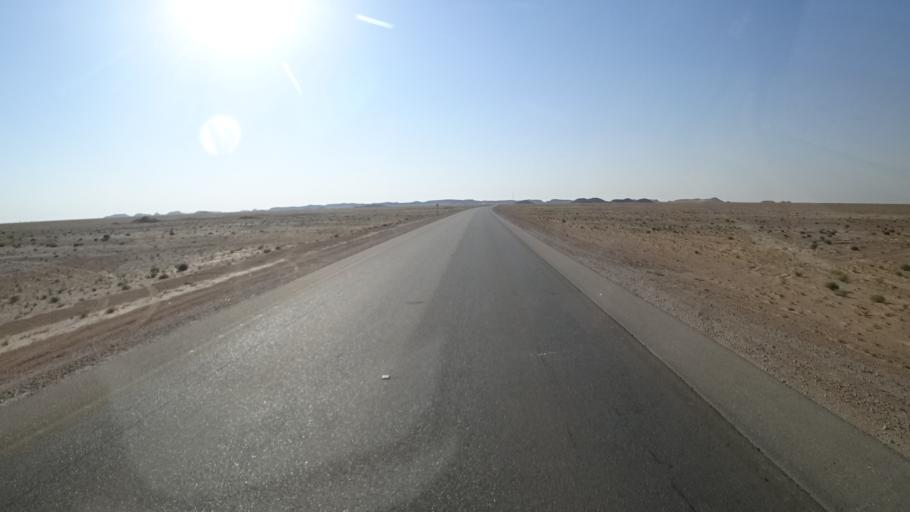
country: OM
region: Zufar
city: Salalah
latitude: 17.6390
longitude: 53.8868
